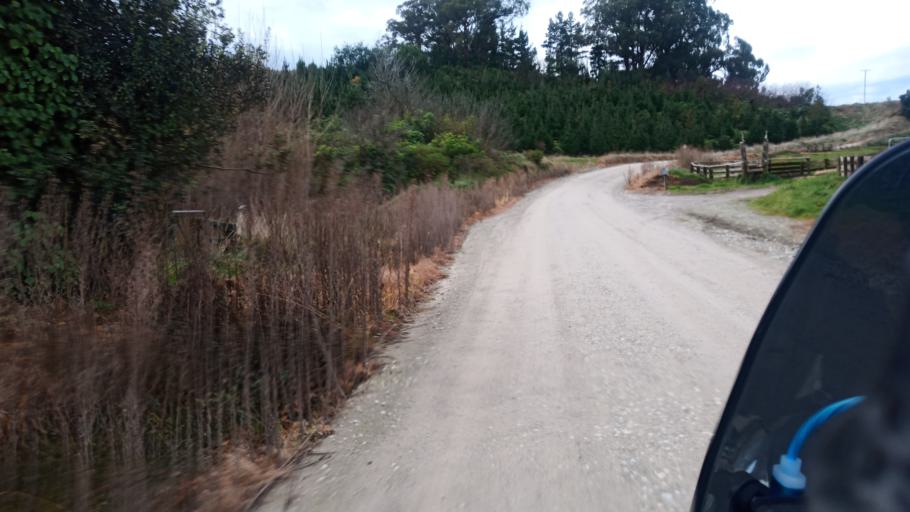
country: NZ
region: Gisborne
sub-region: Gisborne District
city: Gisborne
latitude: -38.3799
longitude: 177.9635
